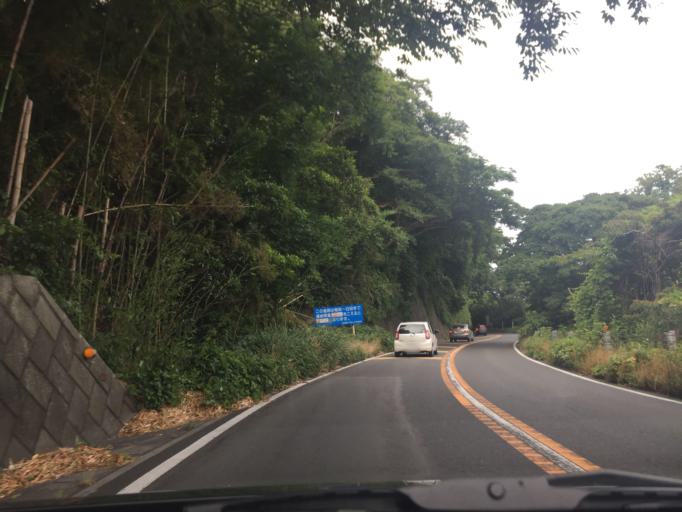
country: JP
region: Shizuoka
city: Shimoda
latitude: 34.7843
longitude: 139.0539
